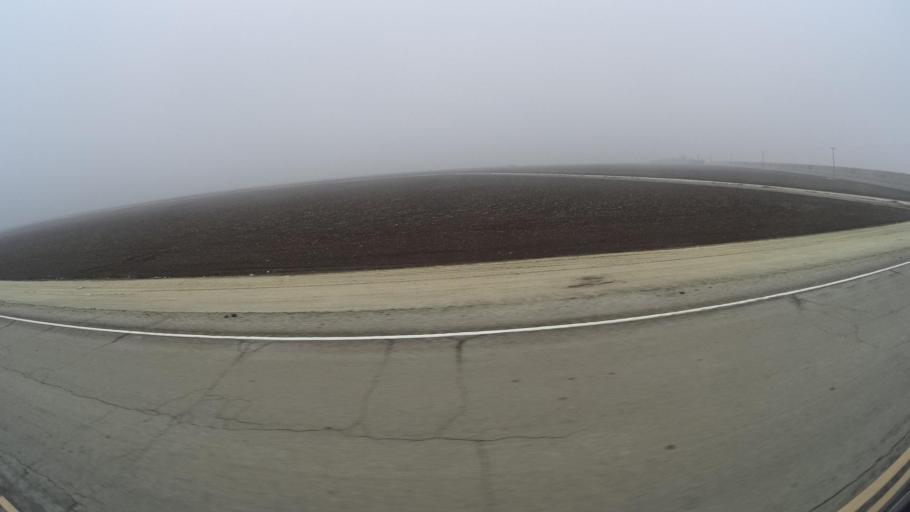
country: US
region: California
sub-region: Kern County
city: Buttonwillow
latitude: 35.4407
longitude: -119.5496
